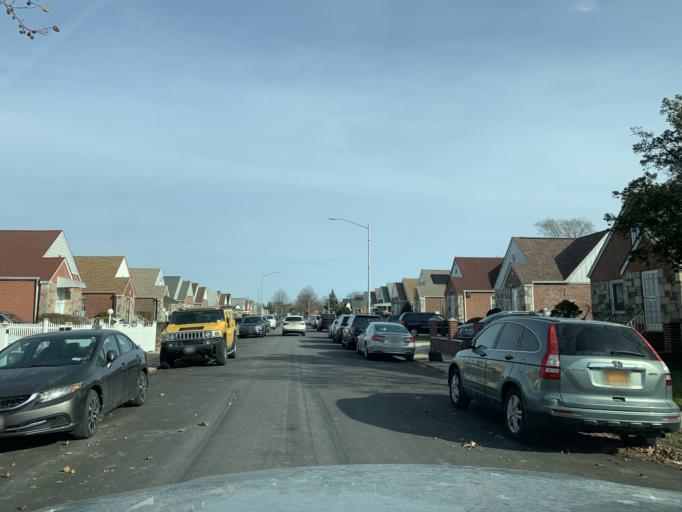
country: US
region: New York
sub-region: Queens County
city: Jamaica
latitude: 40.7019
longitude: -73.7718
